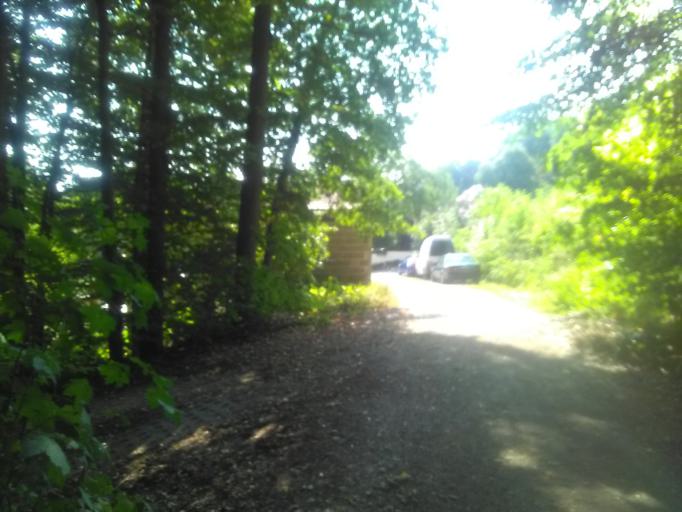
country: DE
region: Bavaria
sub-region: Upper Franconia
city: Bamberg
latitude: 49.8659
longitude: 10.9042
